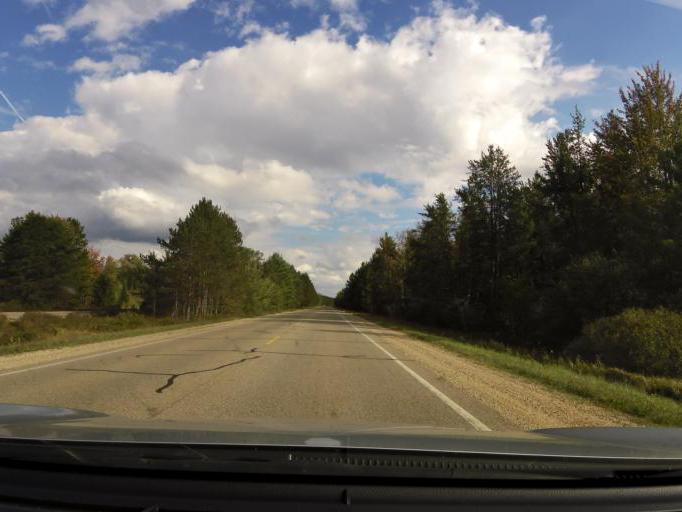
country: US
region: Michigan
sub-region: Roscommon County
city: Saint Helen
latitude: 44.4122
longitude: -84.4623
